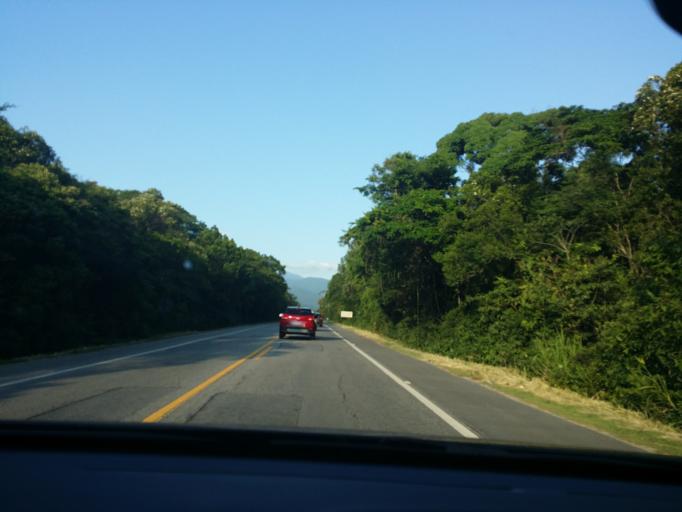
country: BR
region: Sao Paulo
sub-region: Biritiba-Mirim
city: Biritiba Mirim
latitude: -23.7558
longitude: -45.8037
